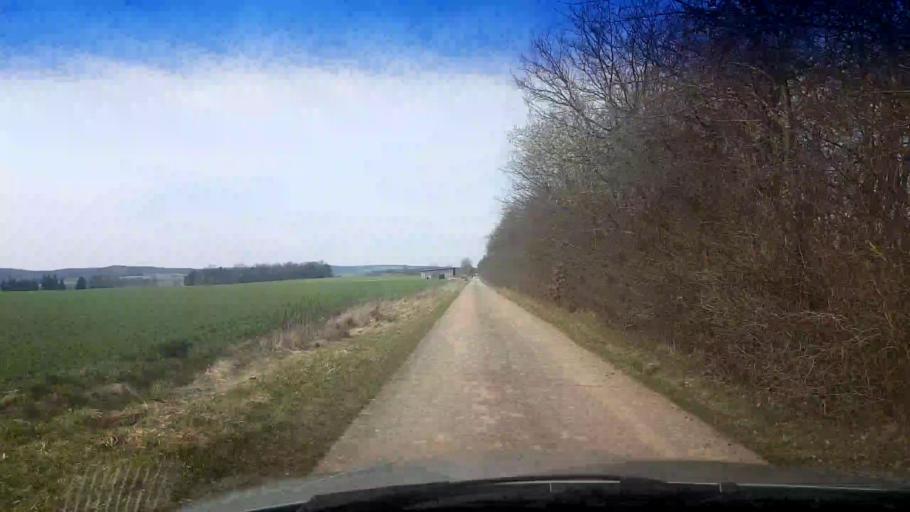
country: DE
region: Bavaria
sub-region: Upper Franconia
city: Burgebrach
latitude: 49.8168
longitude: 10.7568
